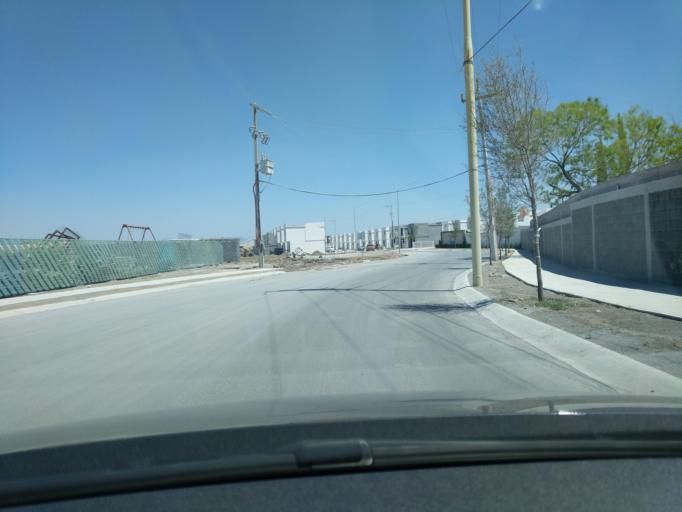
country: MX
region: Nuevo Leon
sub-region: Salinas Victoria
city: Emiliano Zapata
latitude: 25.9100
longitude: -100.2656
